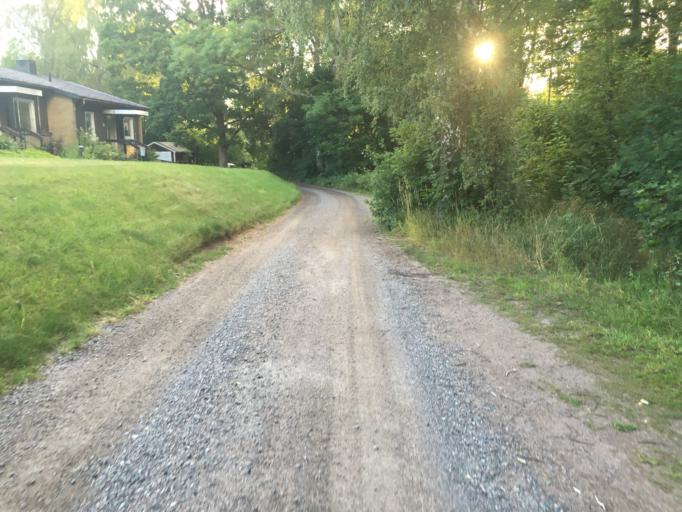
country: SE
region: Kalmar
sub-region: Nybro Kommun
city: Nybro
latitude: 56.9439
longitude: 15.9128
